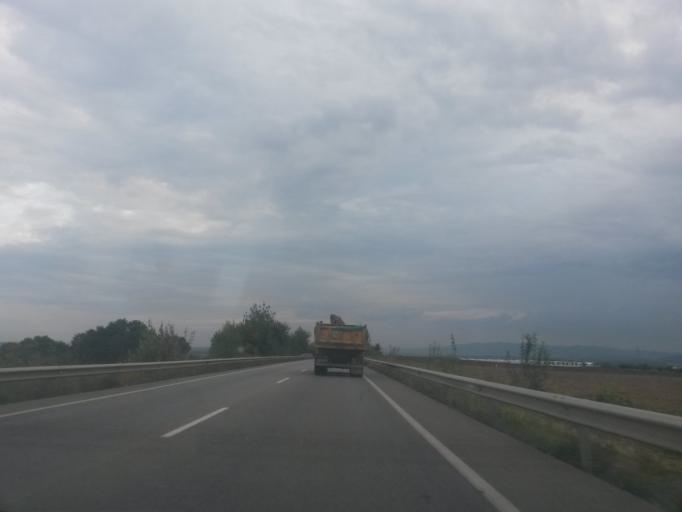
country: ES
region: Catalonia
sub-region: Provincia de Girona
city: Banyoles
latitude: 42.1275
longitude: 2.7781
